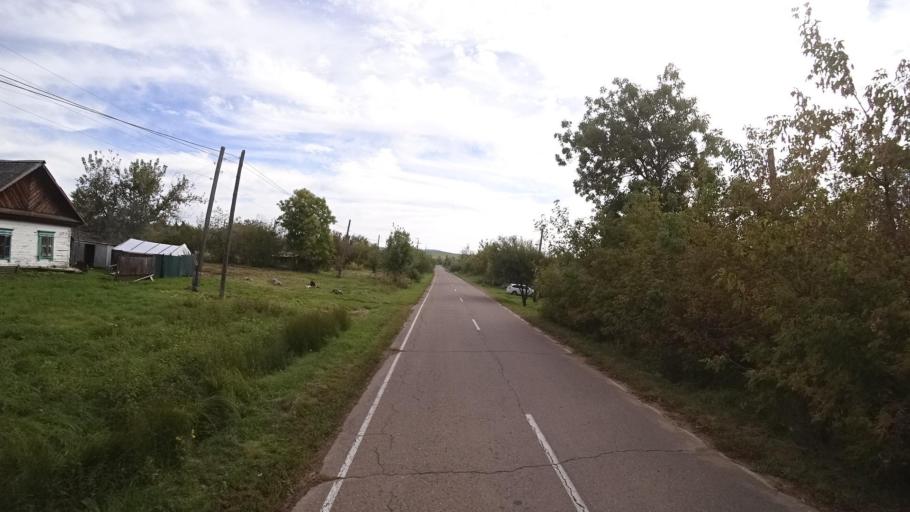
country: RU
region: Primorskiy
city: Dostoyevka
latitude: 44.3256
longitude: 133.4768
